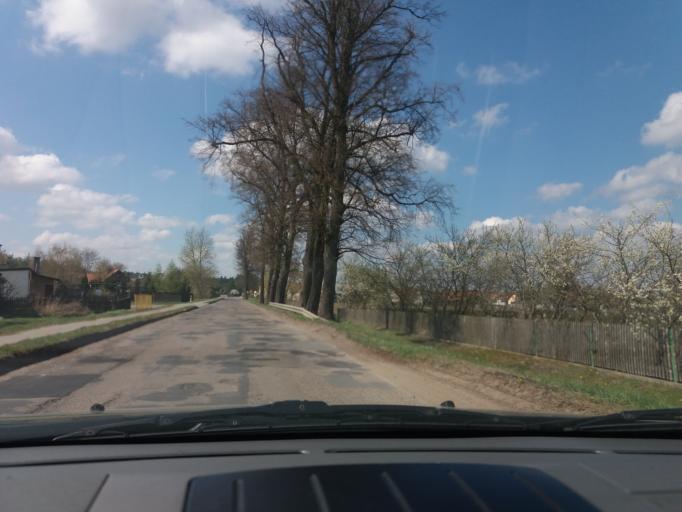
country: PL
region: Warmian-Masurian Voivodeship
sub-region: Powiat szczycienski
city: Jedwabno
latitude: 53.3627
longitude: 20.6396
